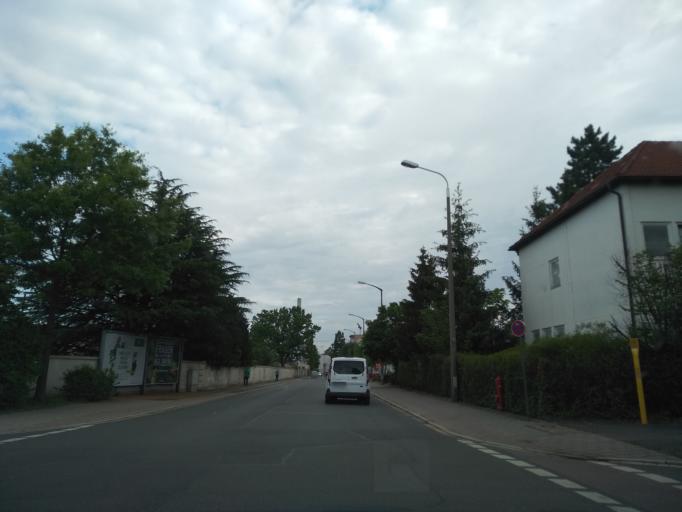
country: DE
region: Bavaria
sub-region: Regierungsbezirk Mittelfranken
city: Erlangen
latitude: 49.5839
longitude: 11.0055
